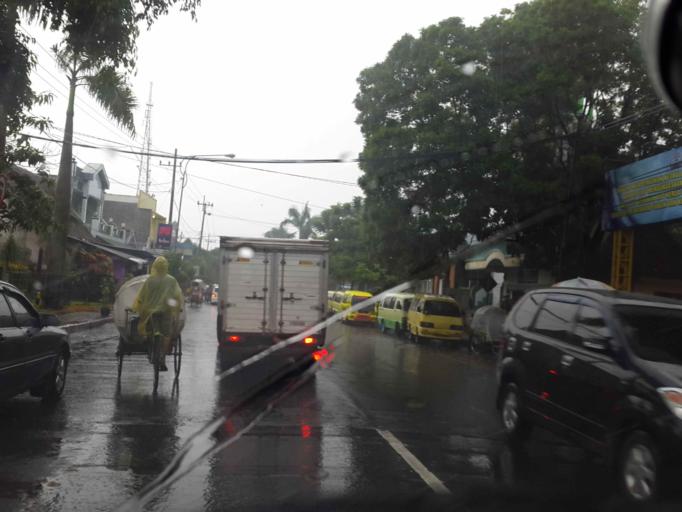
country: ID
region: East Java
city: Kepanjen
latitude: -8.1334
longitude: 112.5734
